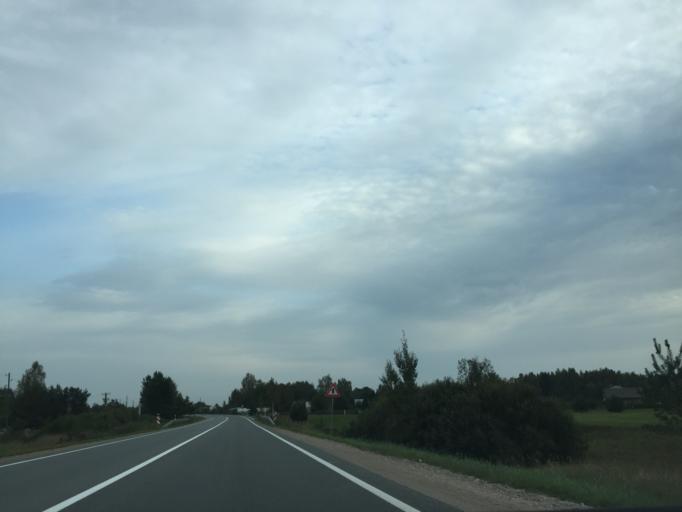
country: LV
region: Kekava
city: Kekava
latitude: 56.8530
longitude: 24.1941
